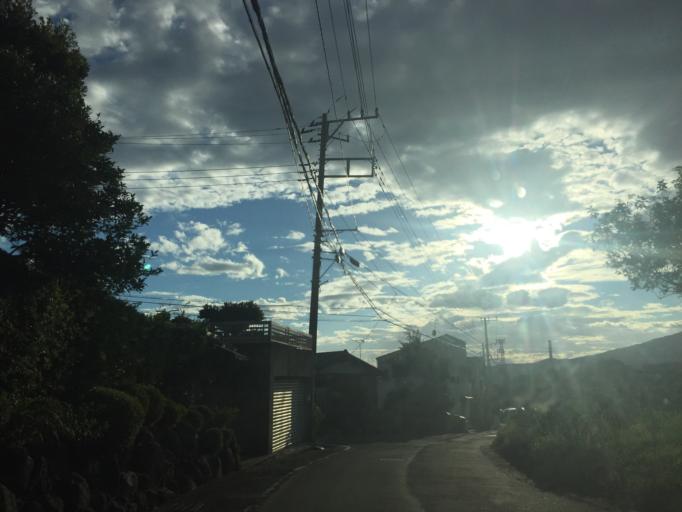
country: JP
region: Shizuoka
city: Mishima
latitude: 35.1579
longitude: 138.9190
